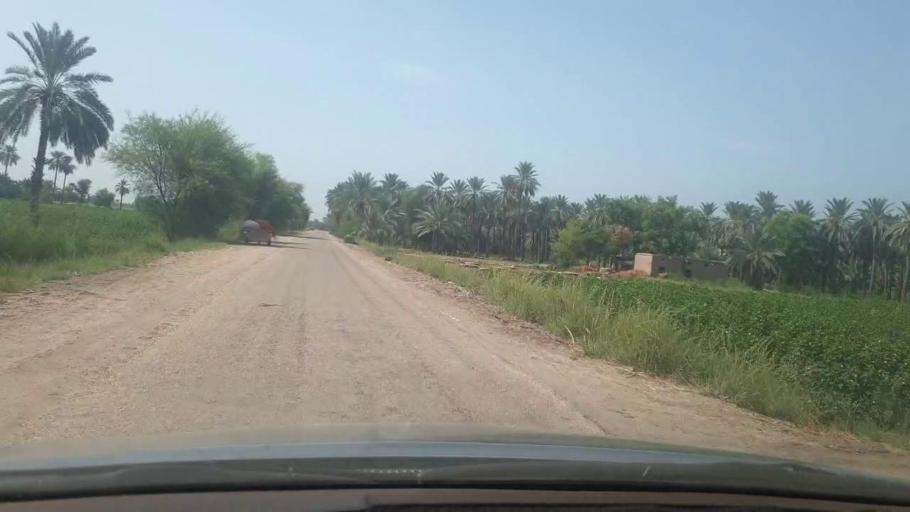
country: PK
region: Sindh
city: Ranipur
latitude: 27.2675
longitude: 68.5817
